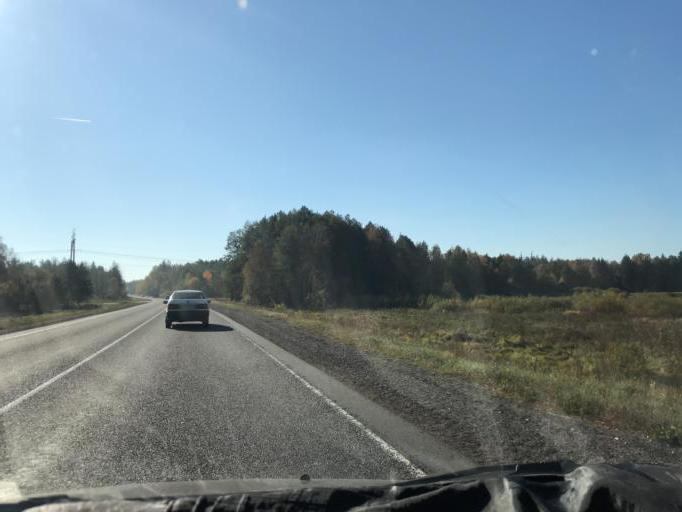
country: BY
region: Mogilev
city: Babruysk
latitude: 53.1737
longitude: 29.0442
